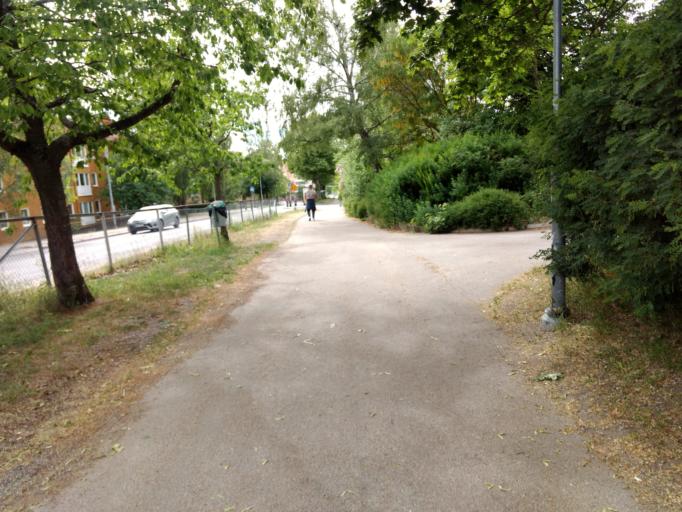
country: SE
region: Stockholm
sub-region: Upplands Vasby Kommun
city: Upplands Vaesby
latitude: 59.5232
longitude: 17.9083
